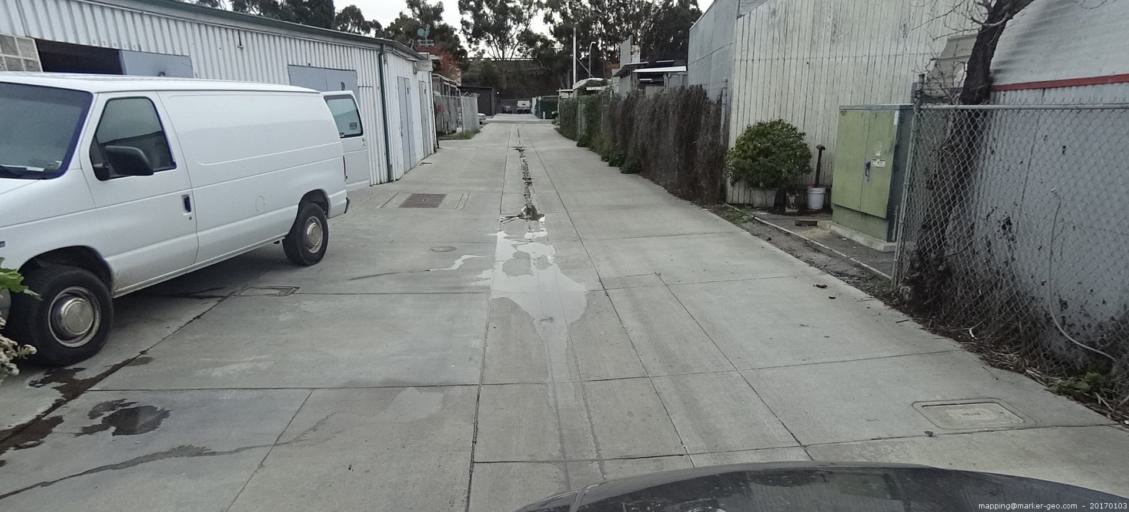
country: US
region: California
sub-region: Orange County
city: Dana Point
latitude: 33.4663
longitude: -117.6795
